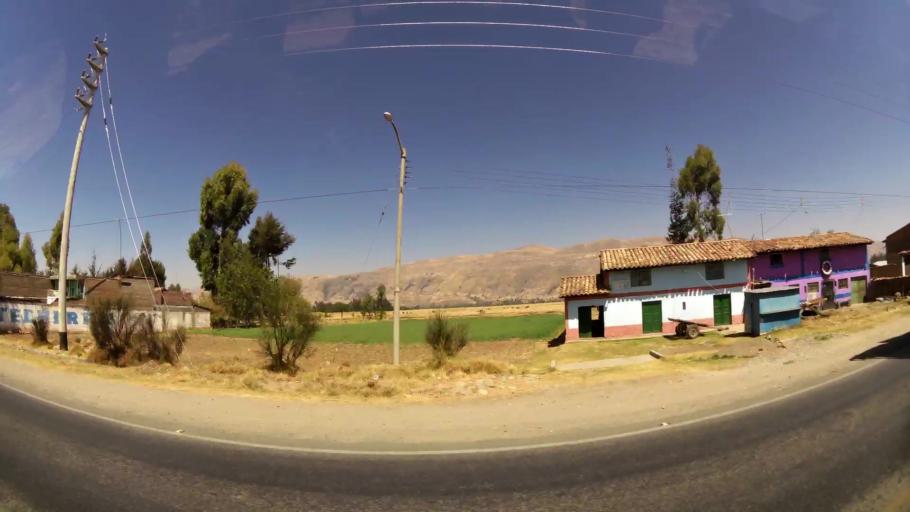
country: PE
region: Junin
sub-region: Provincia de Jauja
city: San Lorenzo
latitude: -11.8324
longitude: -75.3989
